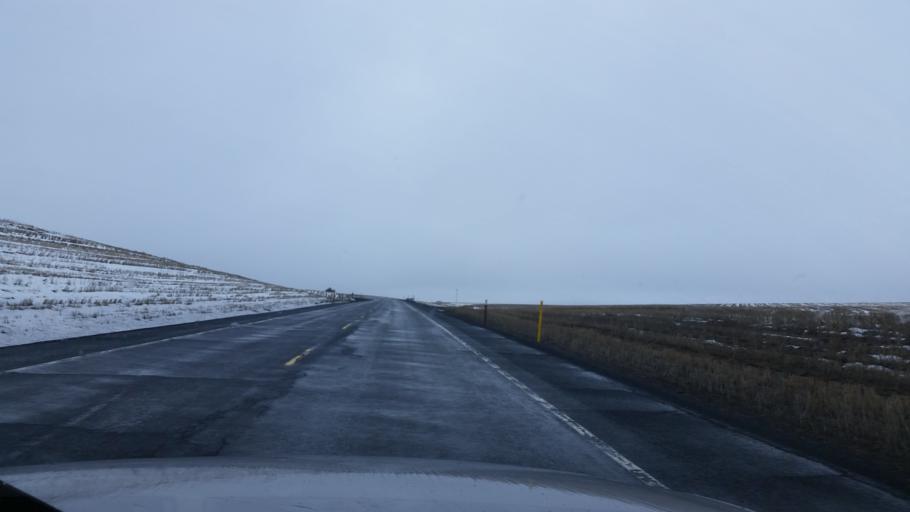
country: US
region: Washington
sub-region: Lincoln County
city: Davenport
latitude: 47.4709
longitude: -118.2895
